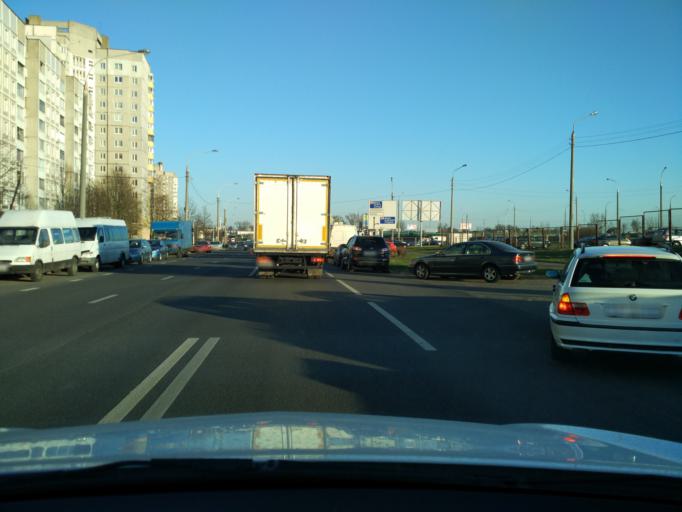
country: BY
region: Minsk
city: Malinovka
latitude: 53.8517
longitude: 27.4369
